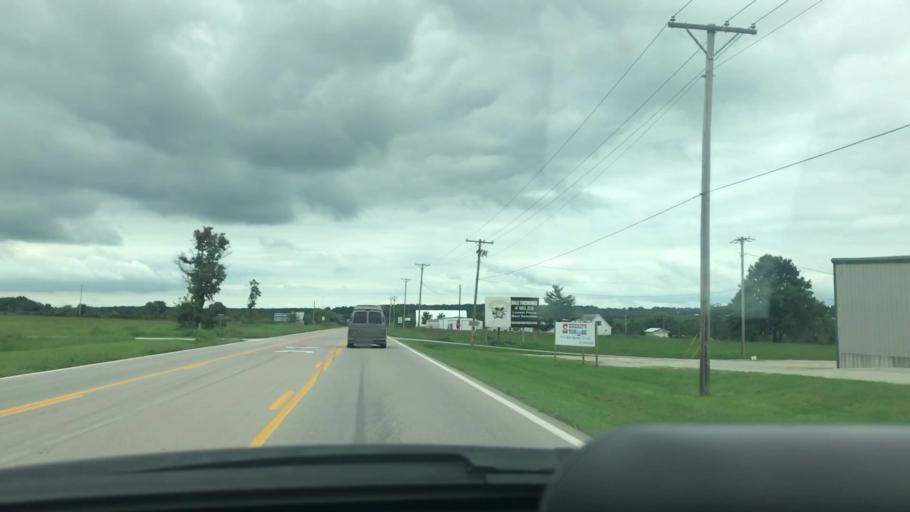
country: US
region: Missouri
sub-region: Dallas County
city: Buffalo
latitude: 37.6562
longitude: -93.1037
